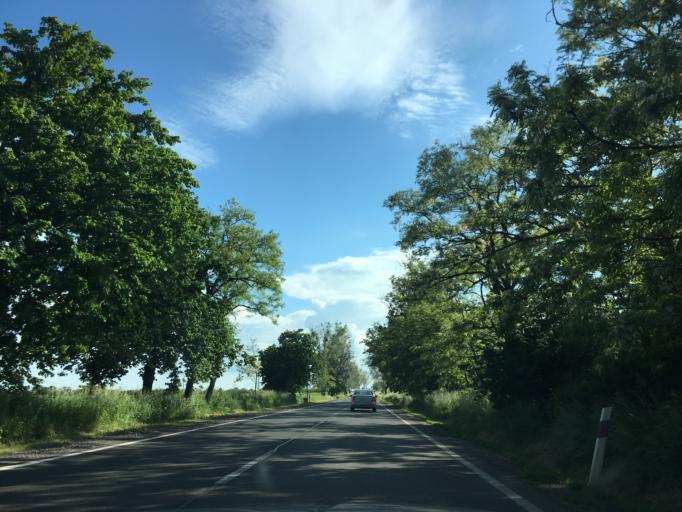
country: HU
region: Borsod-Abauj-Zemplen
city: Tolcsva
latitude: 48.2940
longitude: 21.5123
